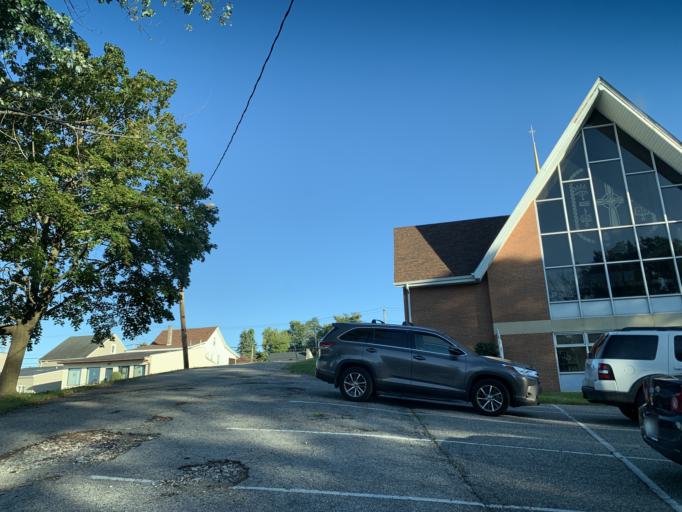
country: US
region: Maryland
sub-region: Baltimore County
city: Perry Hall
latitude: 39.3973
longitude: -76.4834
